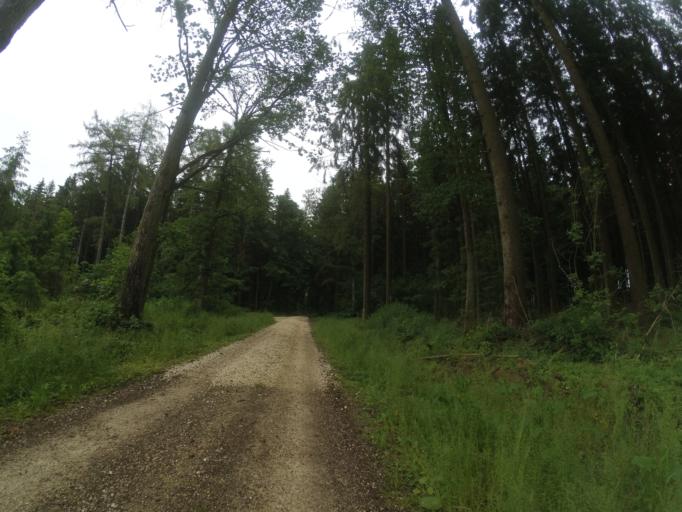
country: DE
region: Baden-Wuerttemberg
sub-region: Tuebingen Region
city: Borslingen
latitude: 48.5141
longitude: 10.0616
